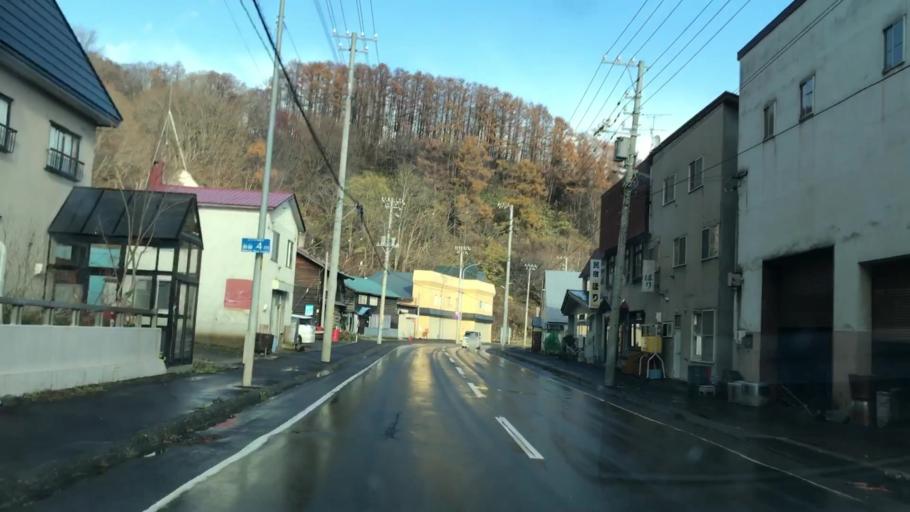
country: JP
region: Hokkaido
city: Yoichi
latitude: 43.2737
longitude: 140.6355
